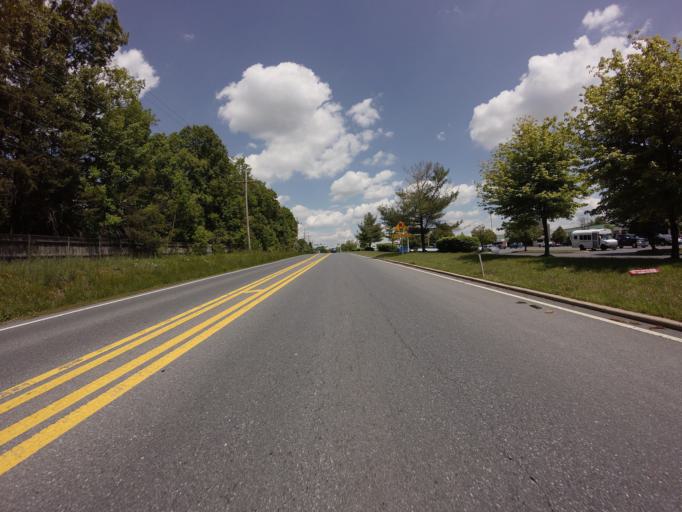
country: US
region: Maryland
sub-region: Frederick County
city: Green Valley
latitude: 39.3441
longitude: -77.2603
